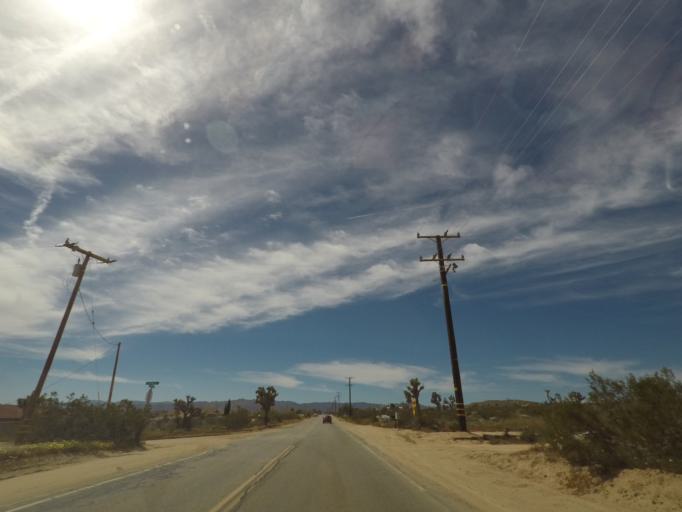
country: US
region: California
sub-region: San Bernardino County
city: Joshua Tree
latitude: 34.1861
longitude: -116.3695
